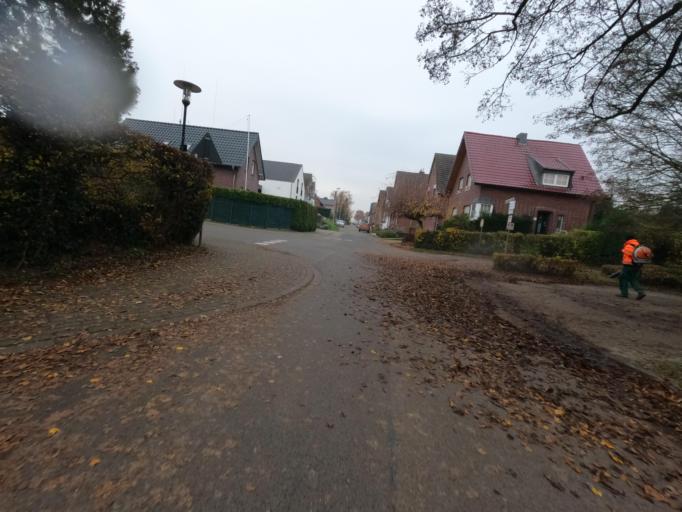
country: DE
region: North Rhine-Westphalia
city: Baesweiler
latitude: 50.9504
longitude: 6.1695
